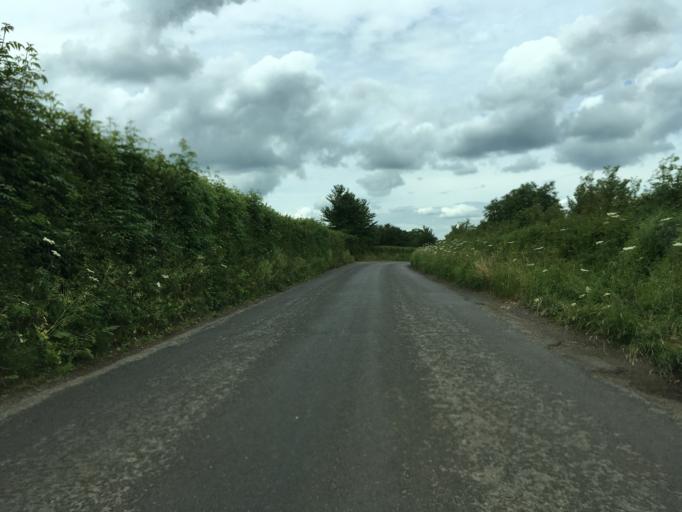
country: GB
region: England
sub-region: Wiltshire
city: Norton
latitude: 51.5388
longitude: -2.1424
